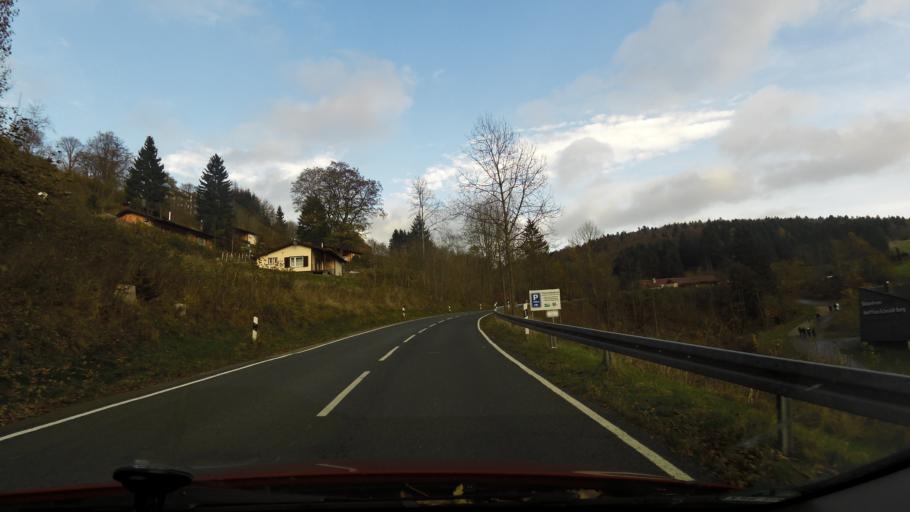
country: DE
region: Lower Saxony
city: Sankt Andreasberg
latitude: 51.7075
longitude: 10.5196
